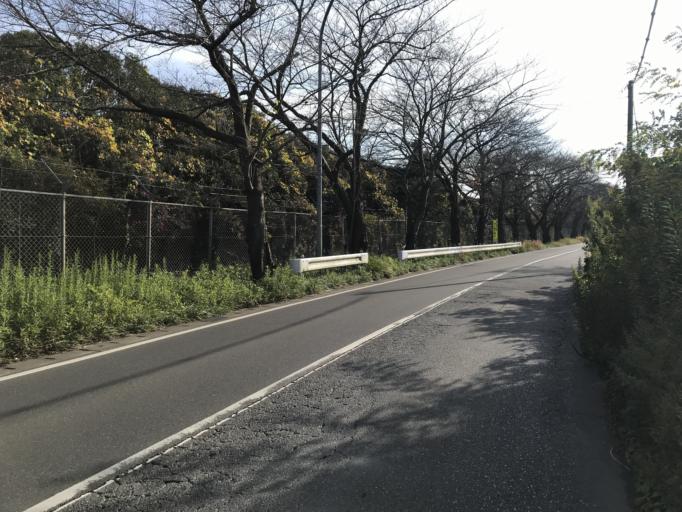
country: JP
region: Chiba
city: Shiroi
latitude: 35.7879
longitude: 140.0103
